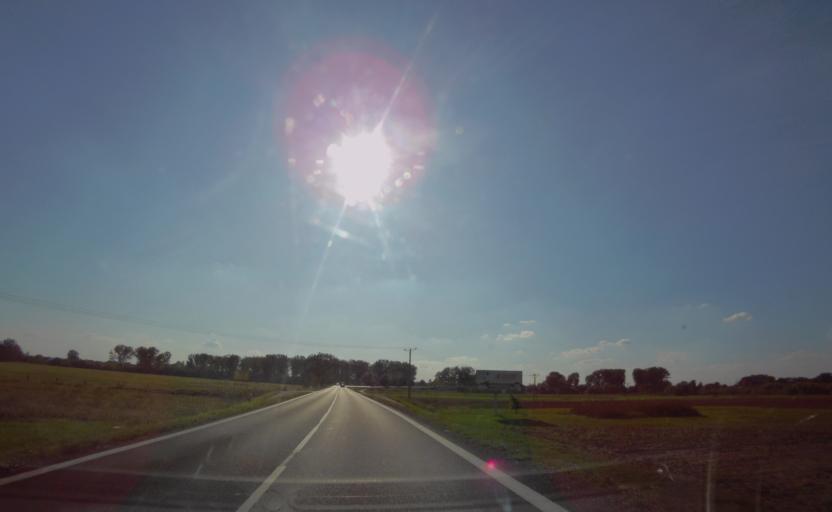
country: PL
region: Subcarpathian Voivodeship
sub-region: Powiat lezajski
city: Kurylowka
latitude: 50.2924
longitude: 22.4491
